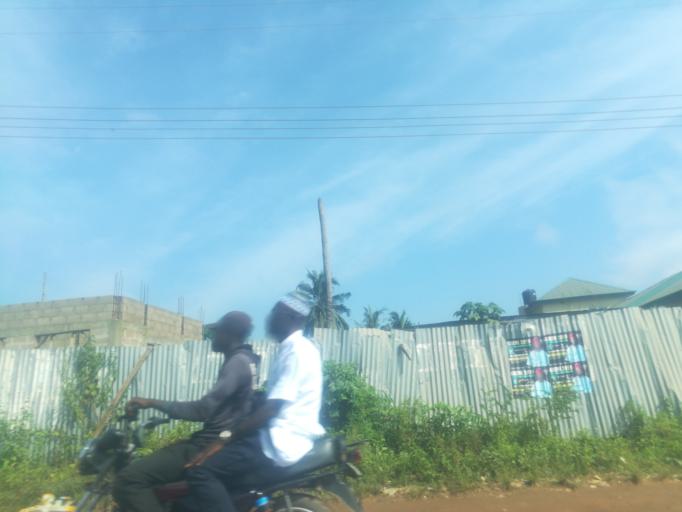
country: NG
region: Oyo
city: Ibadan
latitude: 7.3370
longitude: 3.8514
